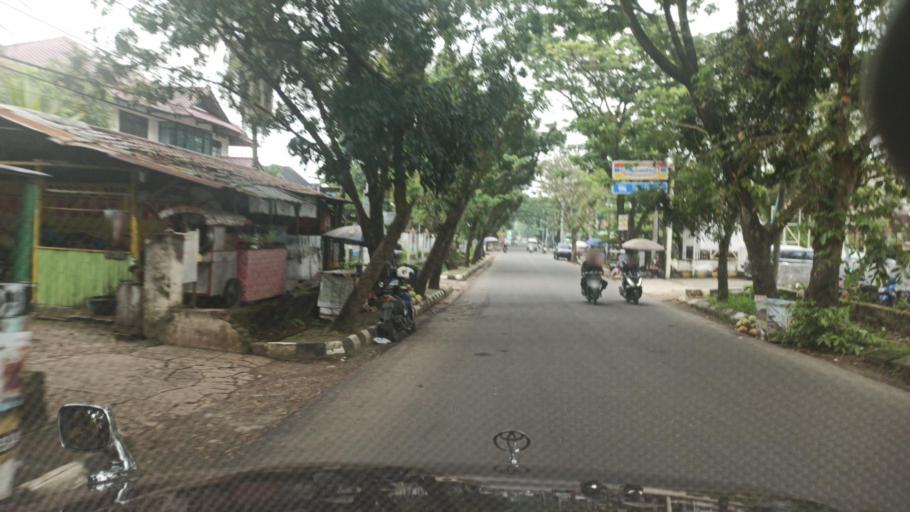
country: ID
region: South Sumatra
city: Plaju
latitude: -2.9947
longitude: 104.7486
